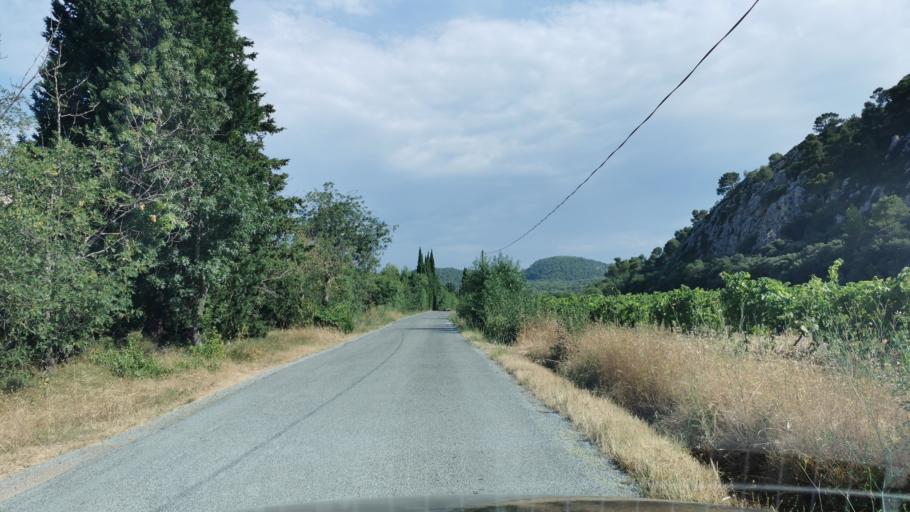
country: FR
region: Languedoc-Roussillon
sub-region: Departement de l'Aude
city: Bize-Minervois
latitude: 43.3325
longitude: 2.8770
